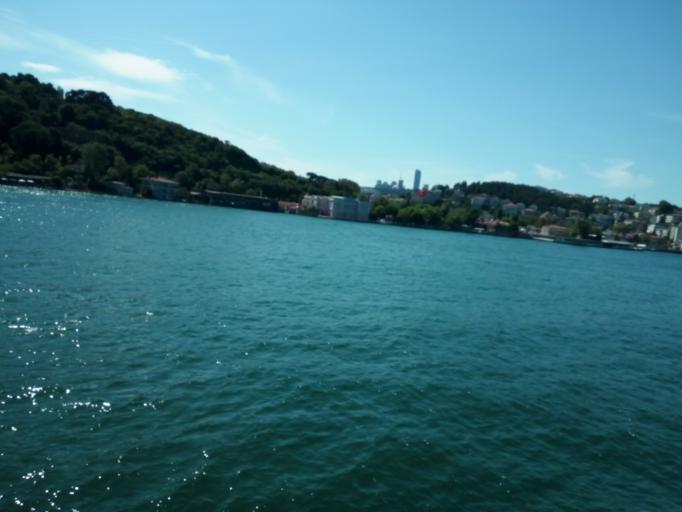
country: TR
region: Istanbul
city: Sisli
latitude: 41.0941
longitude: 29.0579
